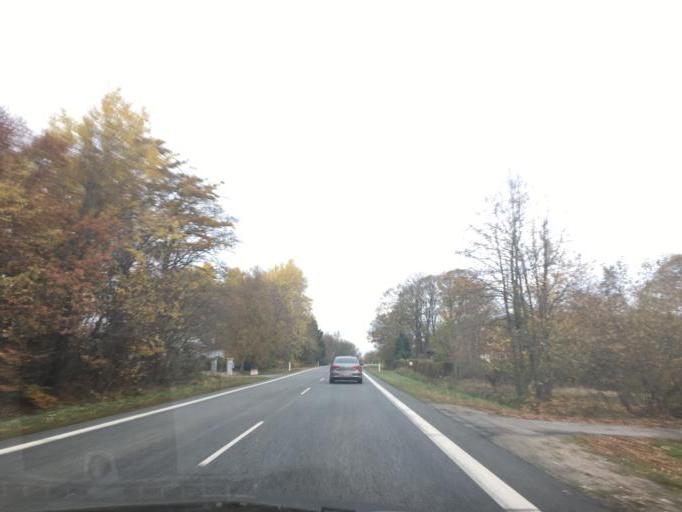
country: DK
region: South Denmark
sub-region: Vejle Kommune
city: Vejle
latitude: 55.6211
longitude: 9.4947
